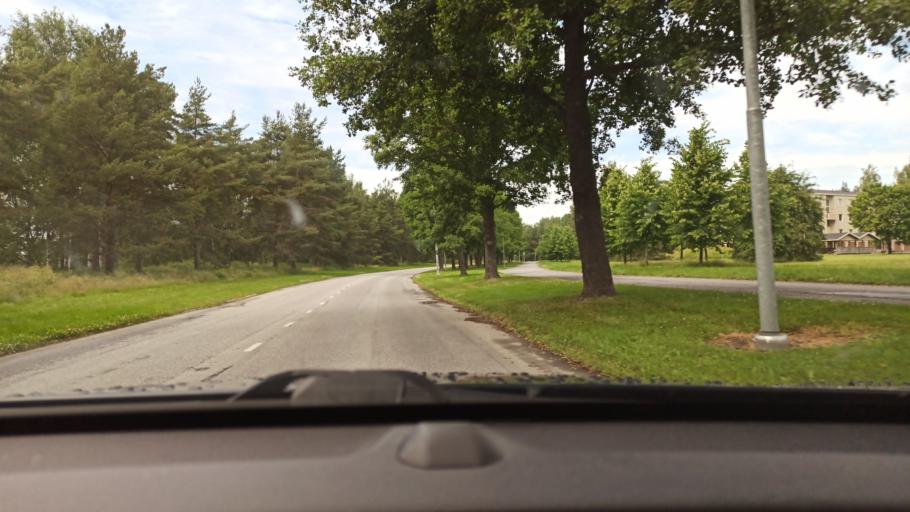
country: FI
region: Satakunta
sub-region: Pori
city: Pori
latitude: 61.5054
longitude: 21.7784
